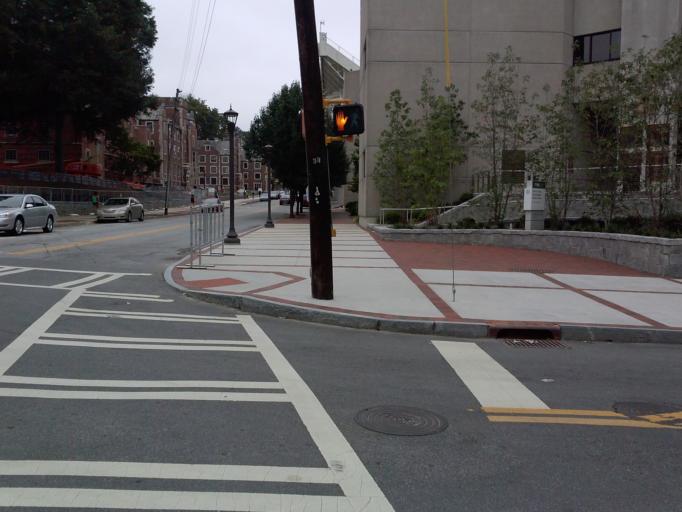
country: US
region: Georgia
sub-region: Fulton County
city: Atlanta
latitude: 33.7740
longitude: -84.3921
